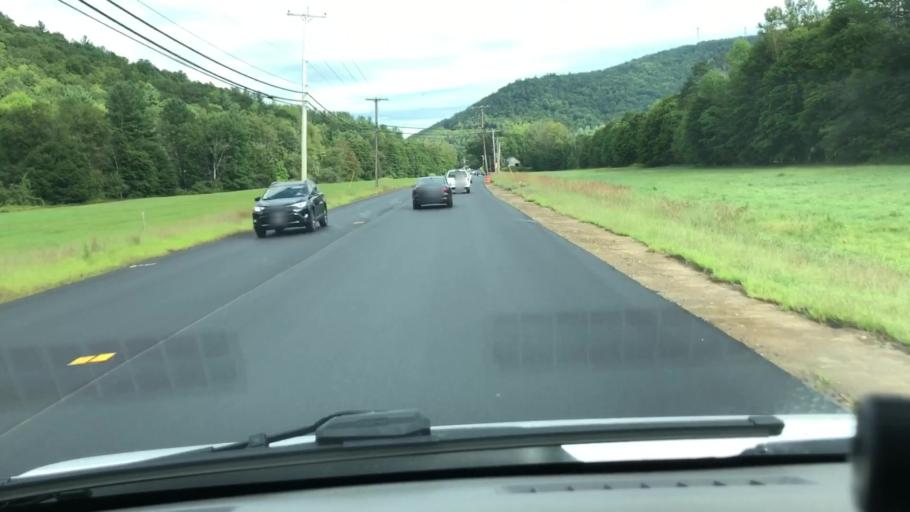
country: US
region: Massachusetts
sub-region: Franklin County
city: Charlemont
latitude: 42.6294
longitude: -72.8909
